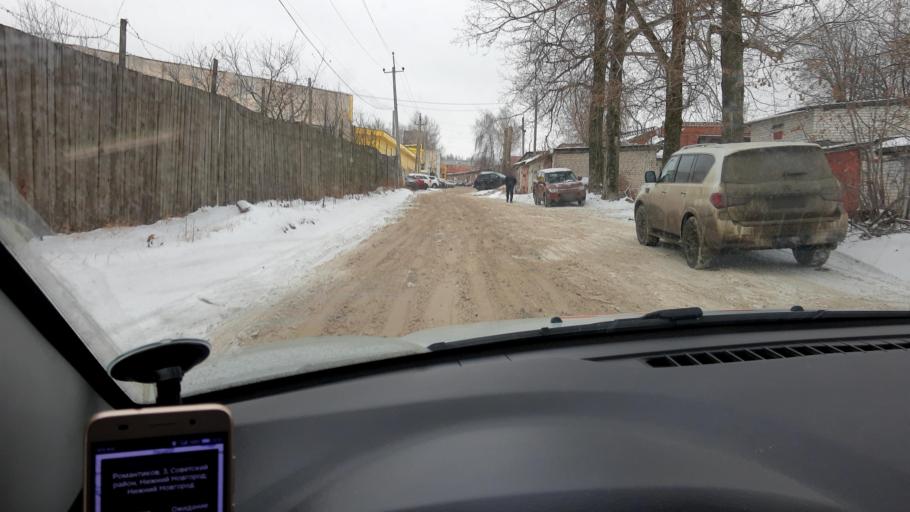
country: RU
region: Nizjnij Novgorod
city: Nizhniy Novgorod
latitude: 56.2481
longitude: 43.9607
